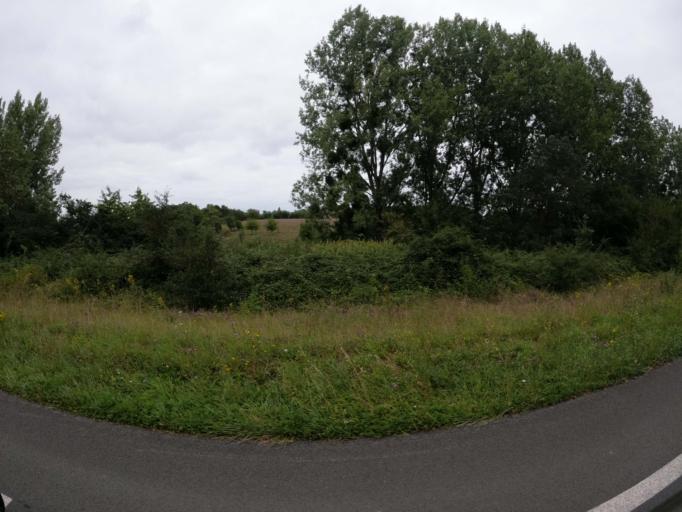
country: FR
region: Pays de la Loire
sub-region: Departement de la Vendee
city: Fontenay-le-Comte
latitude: 46.4567
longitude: -0.8355
